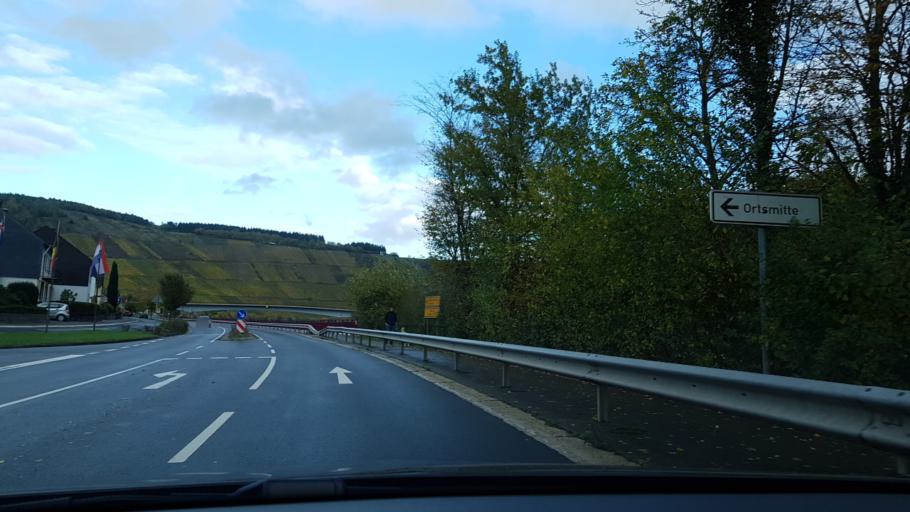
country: DE
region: Rheinland-Pfalz
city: Mehring
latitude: 49.7941
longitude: 6.8244
